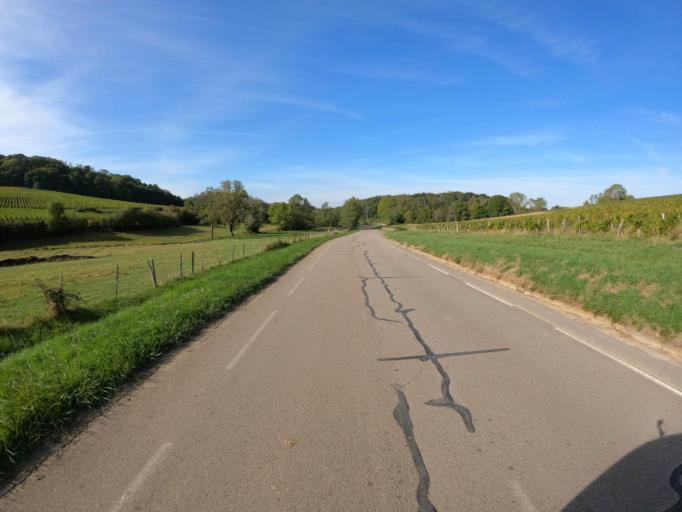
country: FR
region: Franche-Comte
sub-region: Departement du Jura
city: Montmorot
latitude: 46.7092
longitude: 5.5319
